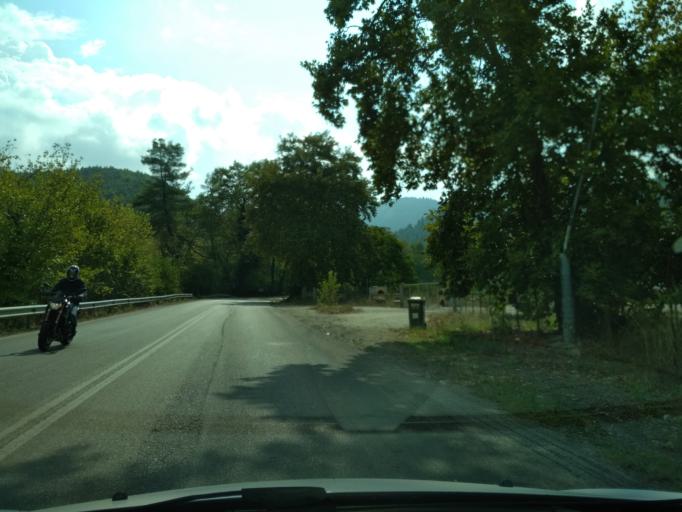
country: GR
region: Central Greece
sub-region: Nomos Evvoias
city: Prokopion
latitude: 38.7208
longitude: 23.5147
